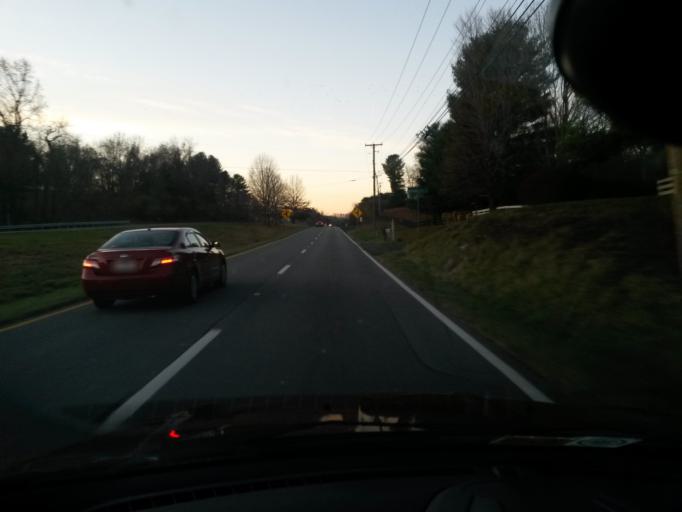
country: US
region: Virginia
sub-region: Botetourt County
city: Fincastle
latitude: 37.4794
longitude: -79.8794
